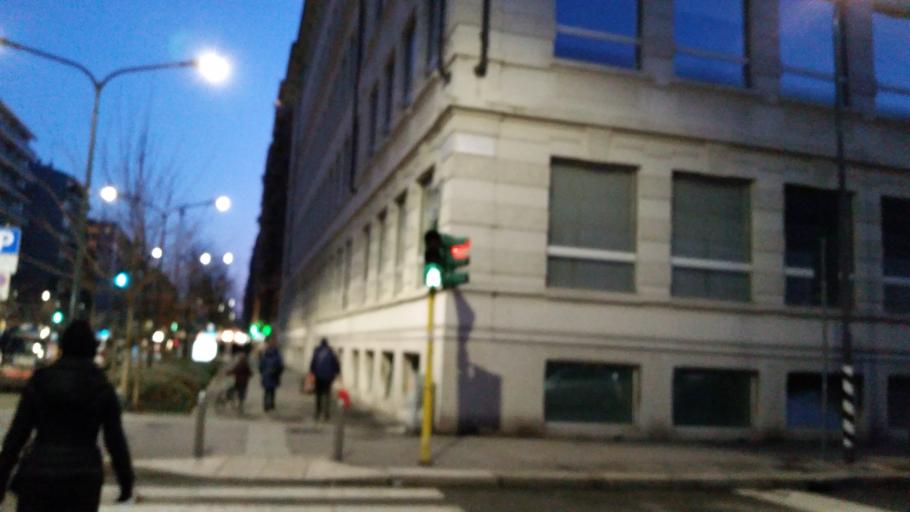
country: IT
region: Lombardy
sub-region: Citta metropolitana di Milano
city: Milano
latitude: 45.4606
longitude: 9.1546
